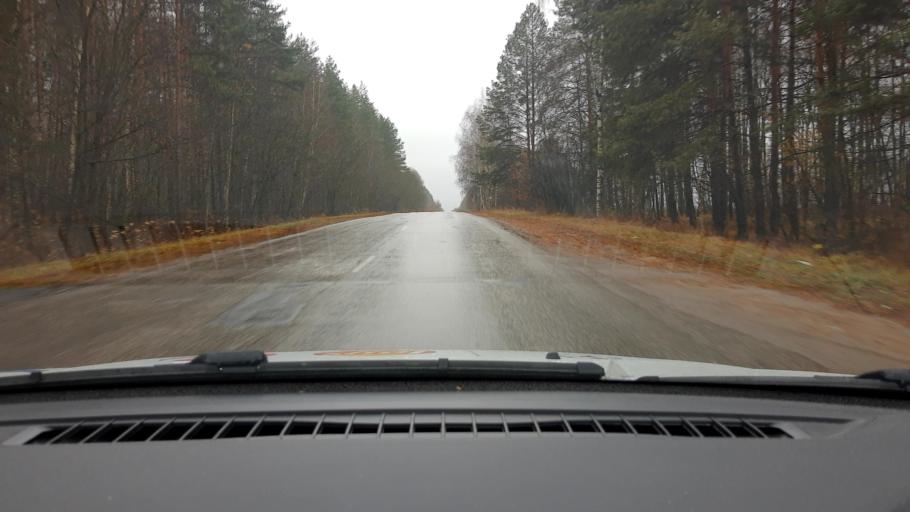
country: RU
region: Nizjnij Novgorod
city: Burevestnik
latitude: 56.0779
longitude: 43.9189
